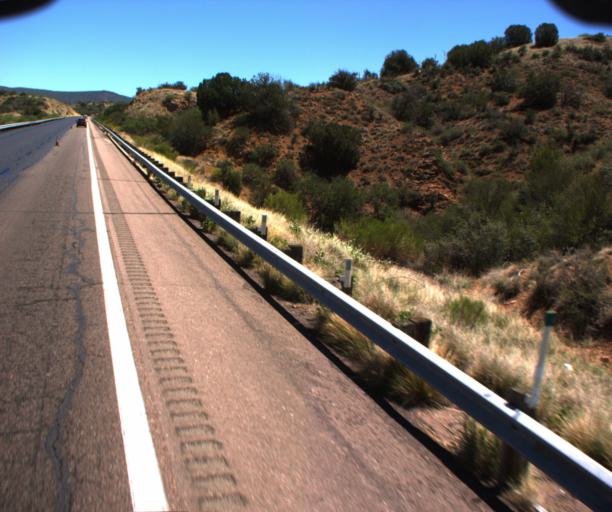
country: US
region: Arizona
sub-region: Gila County
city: Payson
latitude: 34.1186
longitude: -111.3476
